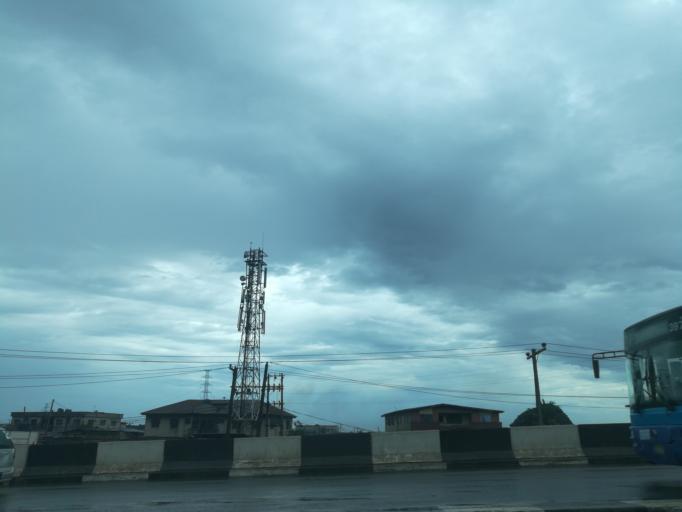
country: NG
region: Lagos
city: Ojota
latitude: 6.6067
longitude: 3.3984
